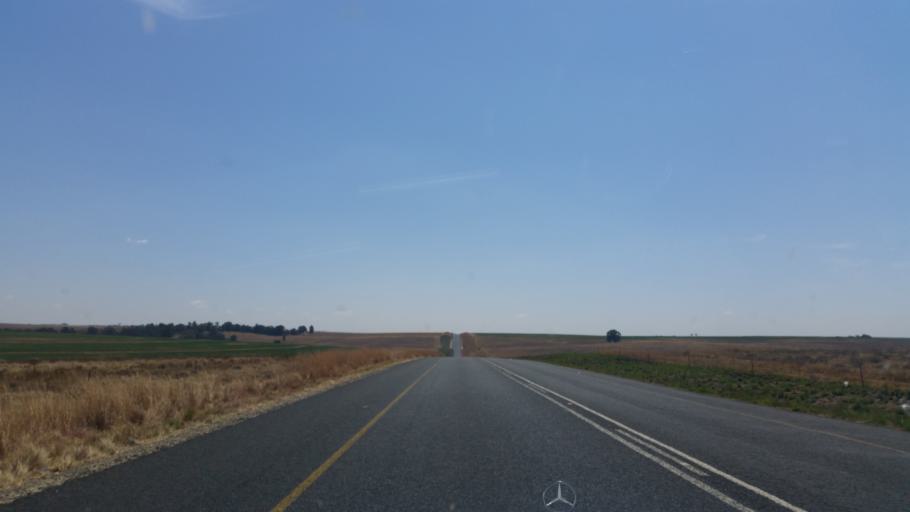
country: ZA
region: Orange Free State
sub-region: Thabo Mofutsanyana District Municipality
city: Phuthaditjhaba
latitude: -28.1832
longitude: 28.6856
